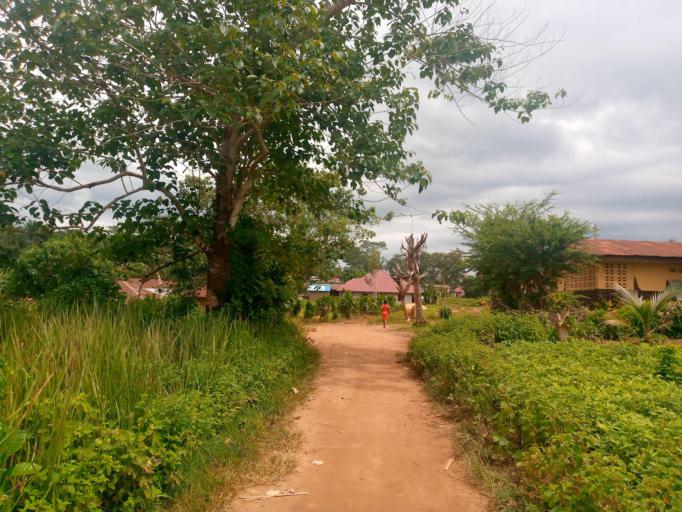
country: SL
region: Southern Province
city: Mogbwemo
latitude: 7.6003
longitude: -12.1707
